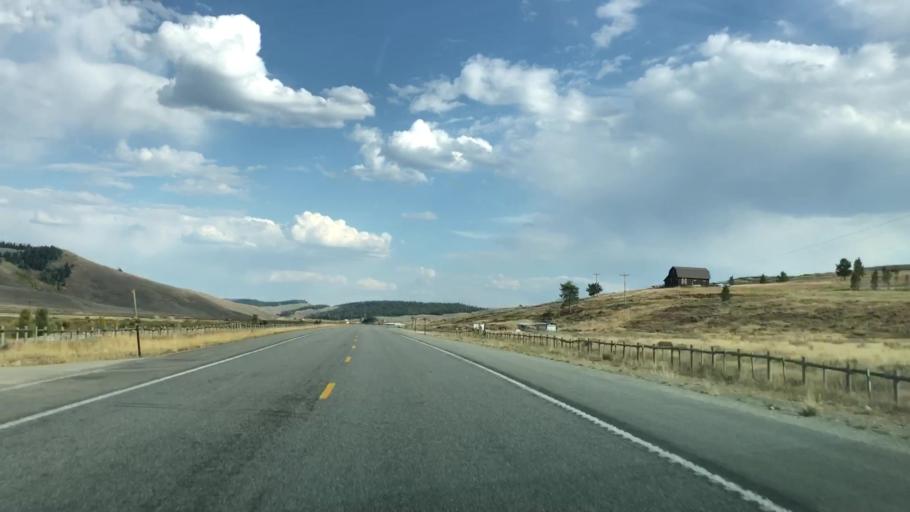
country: US
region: Wyoming
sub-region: Teton County
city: Hoback
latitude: 43.2258
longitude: -110.4314
